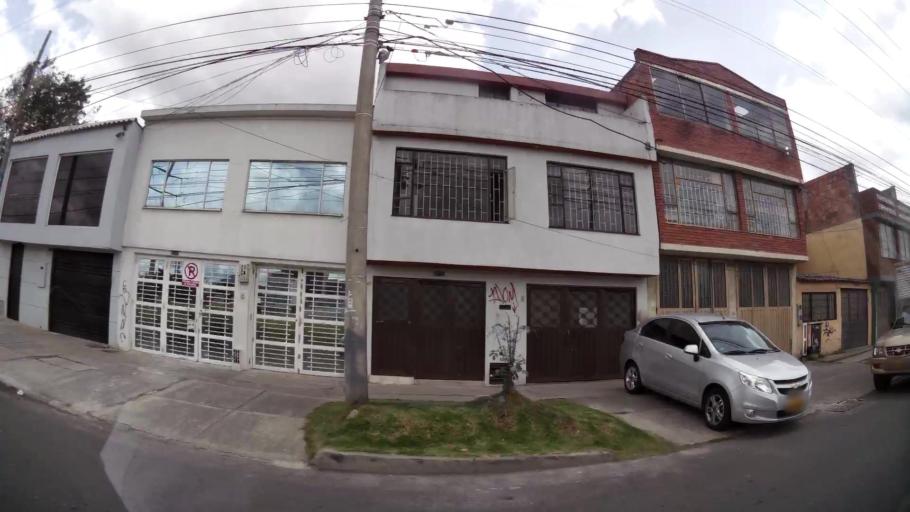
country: CO
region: Bogota D.C.
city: Bogota
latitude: 4.6954
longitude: -74.1174
